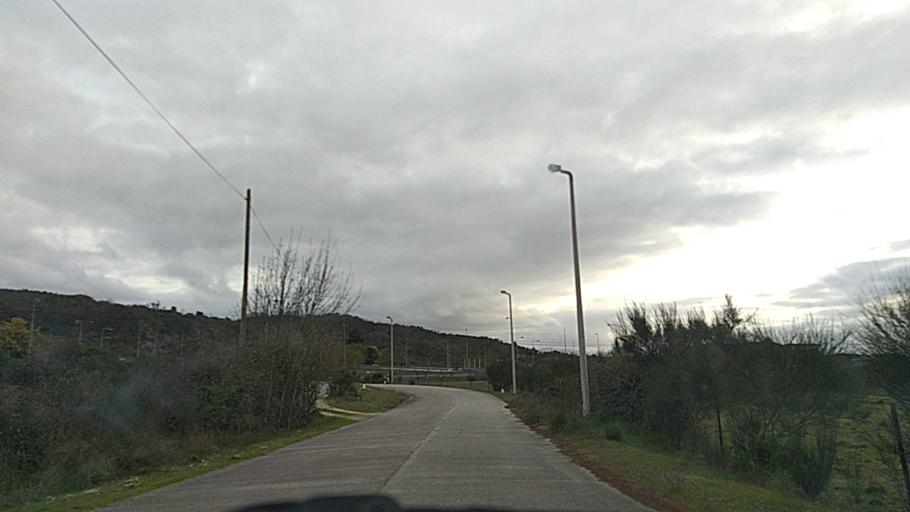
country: PT
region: Guarda
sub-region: Celorico da Beira
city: Celorico da Beira
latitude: 40.6319
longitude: -7.4134
